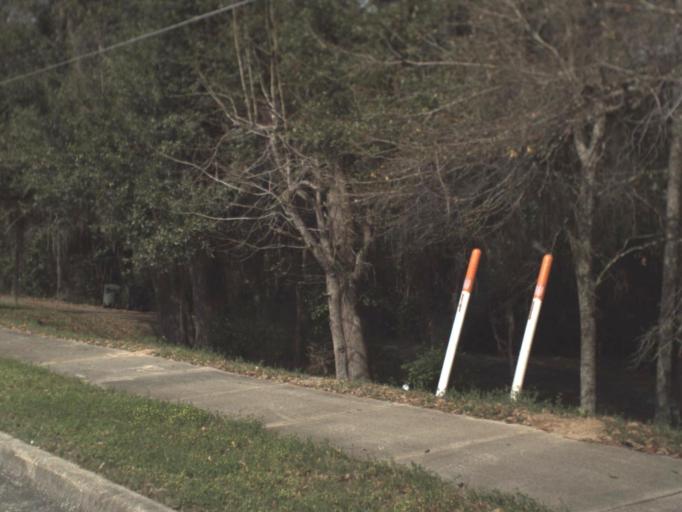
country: US
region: Florida
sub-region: Leon County
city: Tallahassee
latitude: 30.4547
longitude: -84.2431
